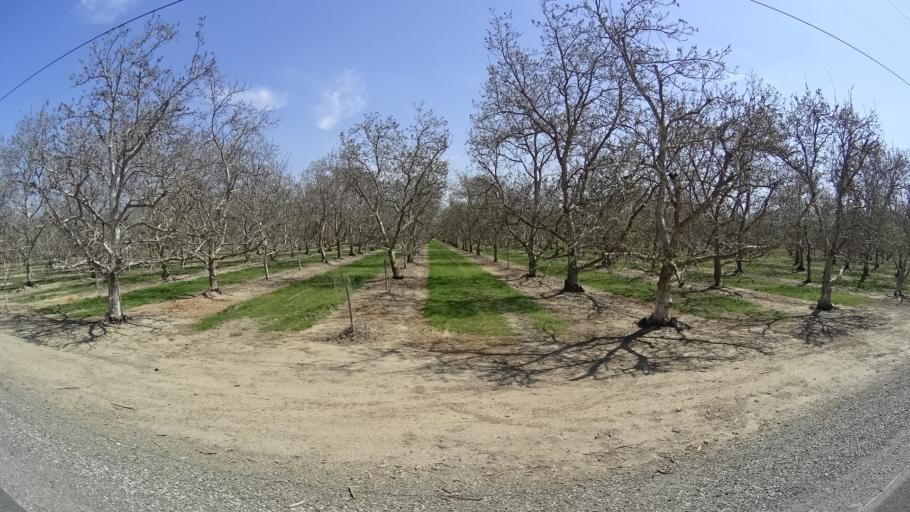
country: US
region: California
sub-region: Glenn County
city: Willows
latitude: 39.4682
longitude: -122.0195
